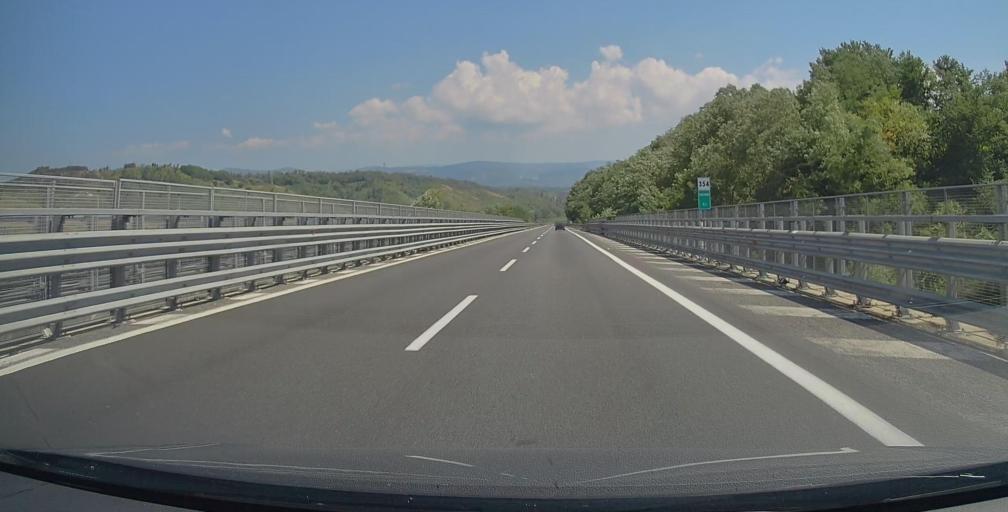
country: IT
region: Calabria
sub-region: Provincia di Vibo-Valentia
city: Maierato
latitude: 38.6726
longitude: 16.1801
